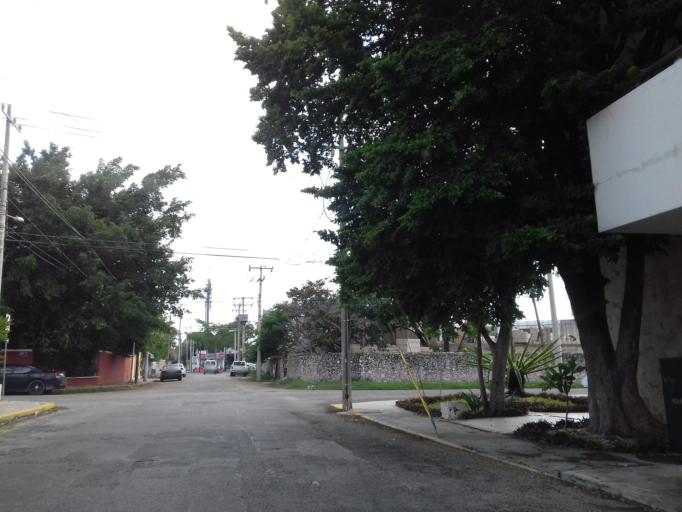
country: MX
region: Yucatan
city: Merida
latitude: 20.9998
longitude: -89.6149
